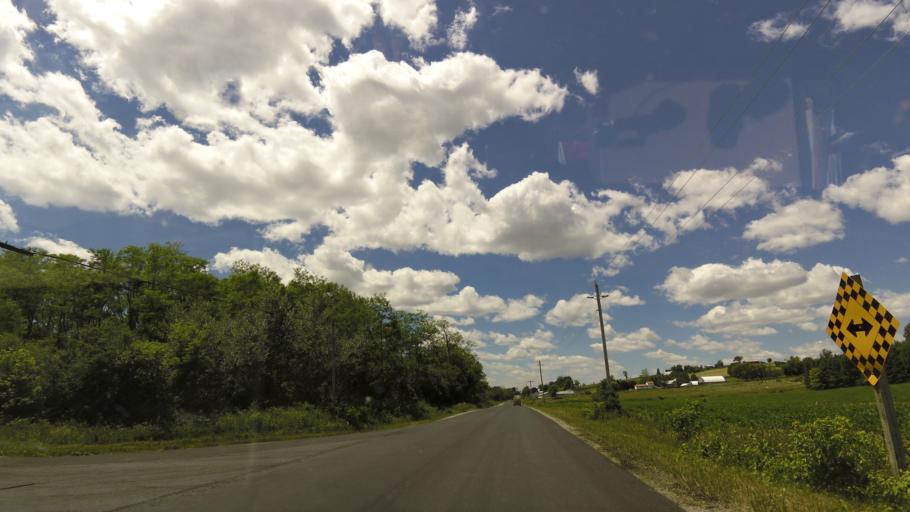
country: CA
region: Ontario
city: Oshawa
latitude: 43.9699
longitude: -78.5278
